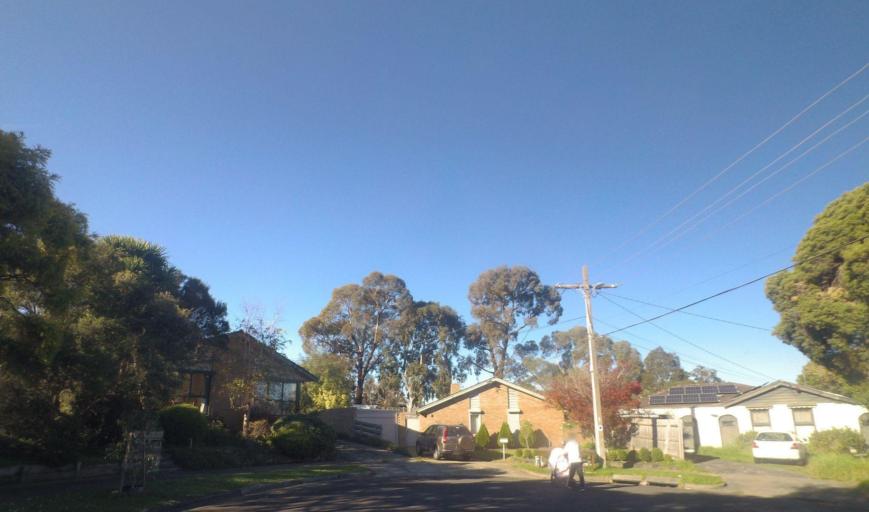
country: AU
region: Victoria
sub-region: Whitehorse
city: Blackburn North
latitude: -37.8107
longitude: 145.1476
